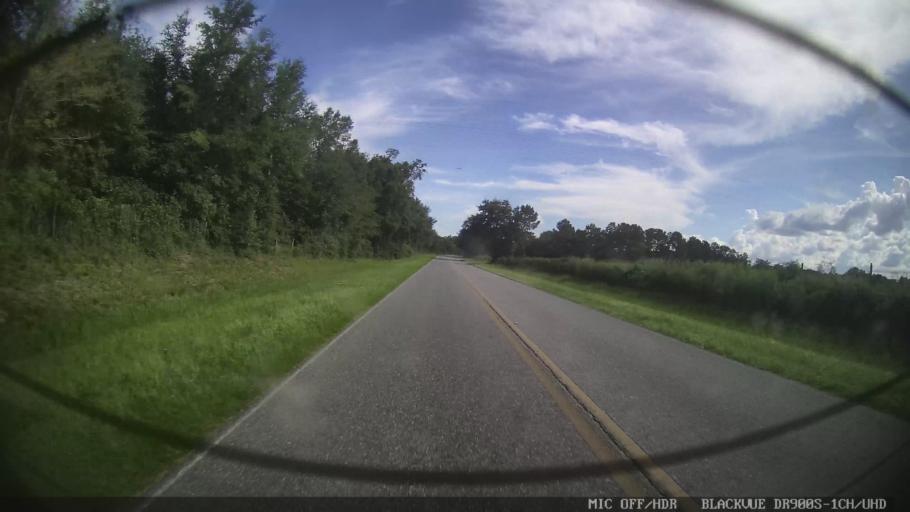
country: US
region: Georgia
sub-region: Echols County
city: Statenville
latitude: 30.6135
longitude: -83.2179
